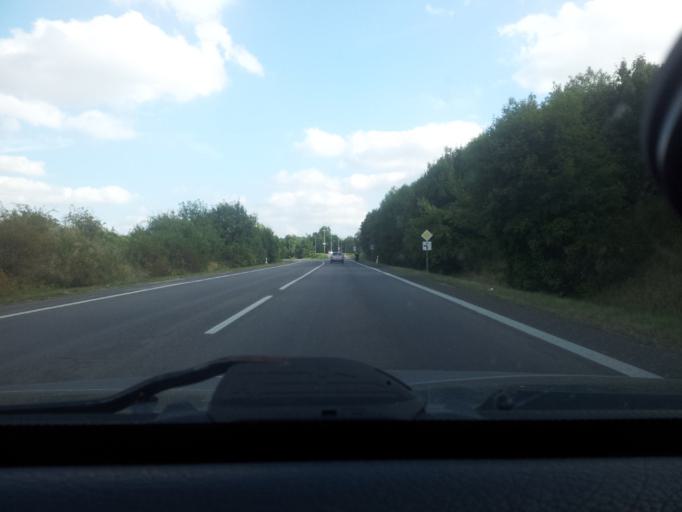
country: SK
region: Nitriansky
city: Levice
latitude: 48.2251
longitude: 18.6129
